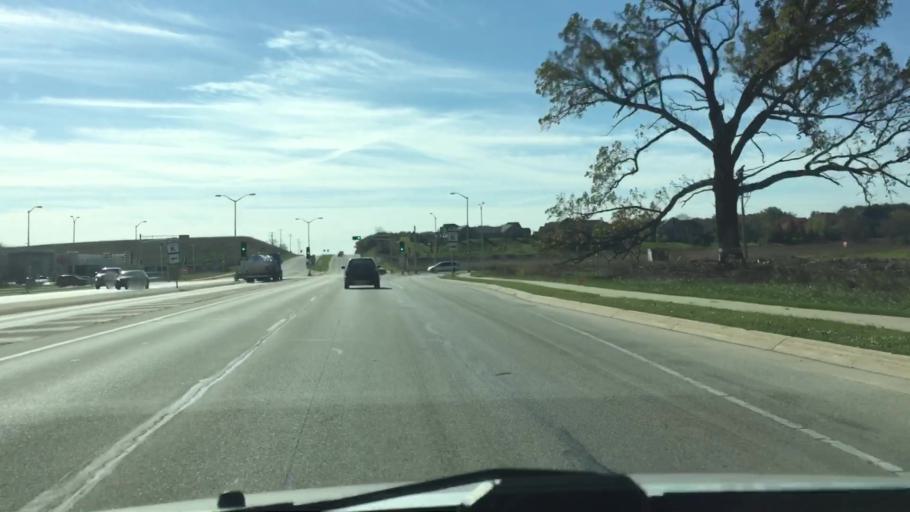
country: US
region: Wisconsin
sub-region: Waukesha County
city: Sussex
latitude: 43.1133
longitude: -88.2448
